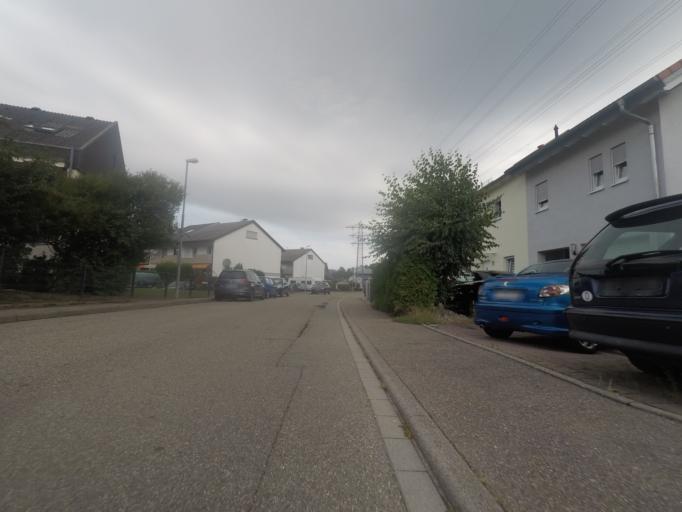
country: DE
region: Baden-Wuerttemberg
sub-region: Karlsruhe Region
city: Gernsbach
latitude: 48.7715
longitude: 8.3454
